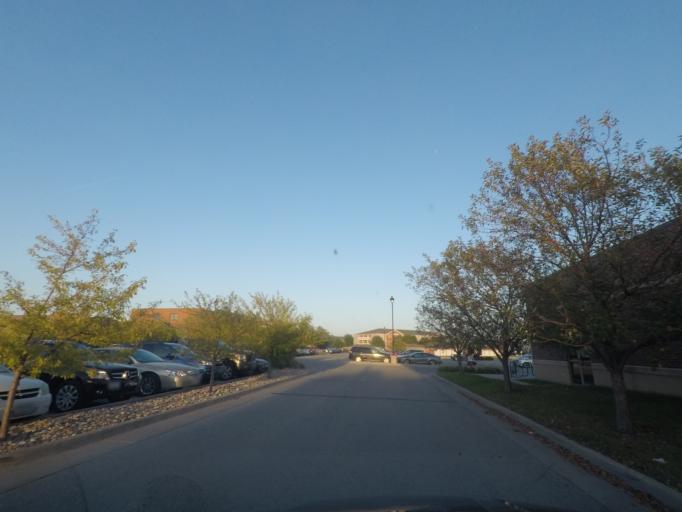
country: US
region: Iowa
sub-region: Story County
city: Ames
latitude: 42.0483
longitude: -93.6443
